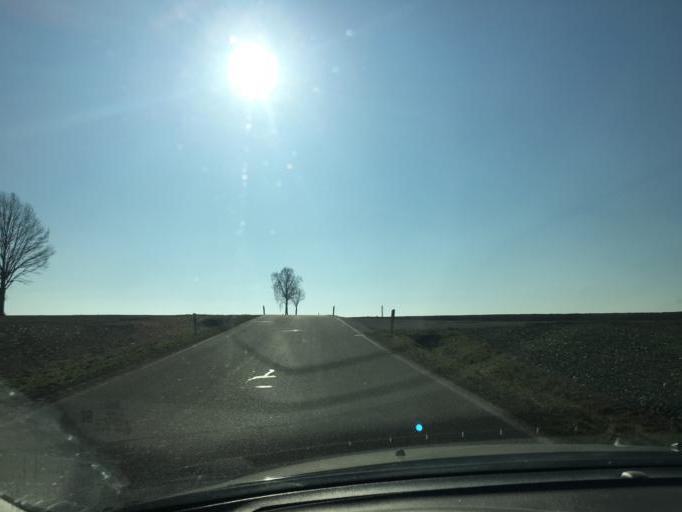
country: DE
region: Saxony
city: Narsdorf
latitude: 51.0244
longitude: 12.7097
